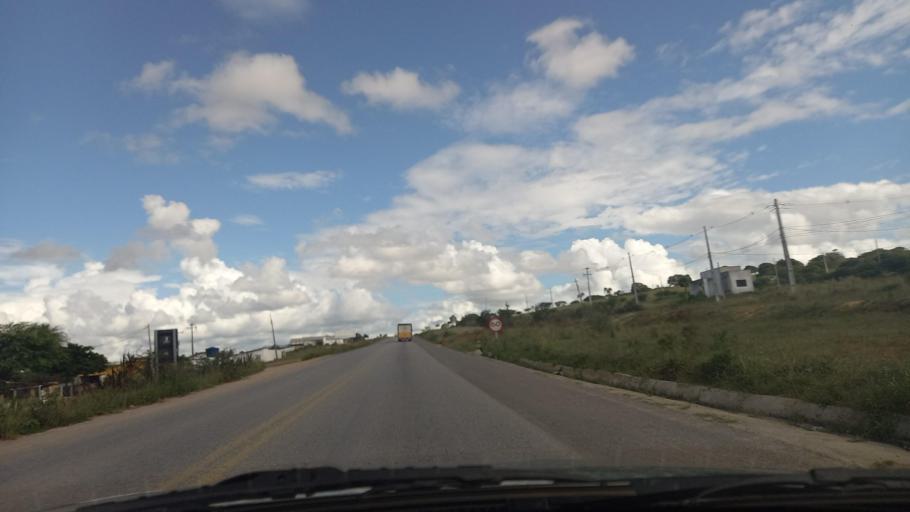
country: BR
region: Pernambuco
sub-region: Sao Joao
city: Sao Joao
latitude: -8.7571
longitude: -36.4306
